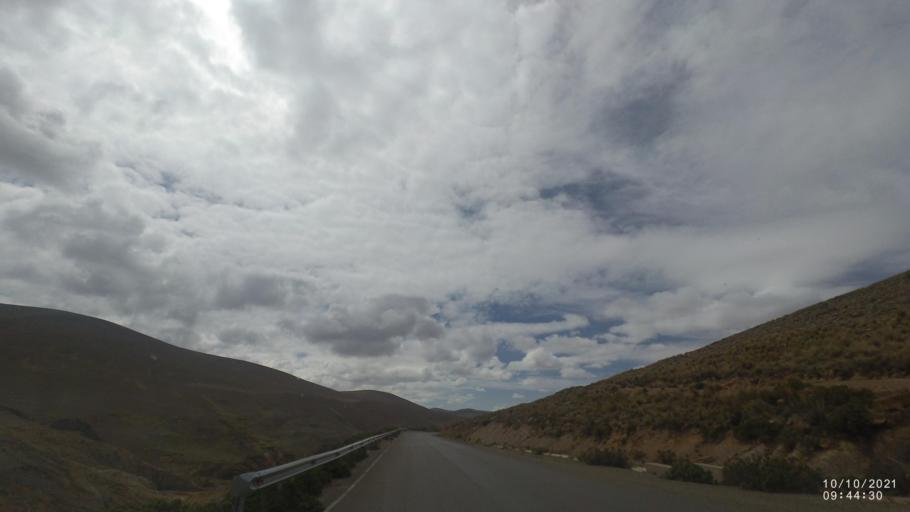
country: BO
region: La Paz
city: Quime
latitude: -17.1609
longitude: -67.3369
